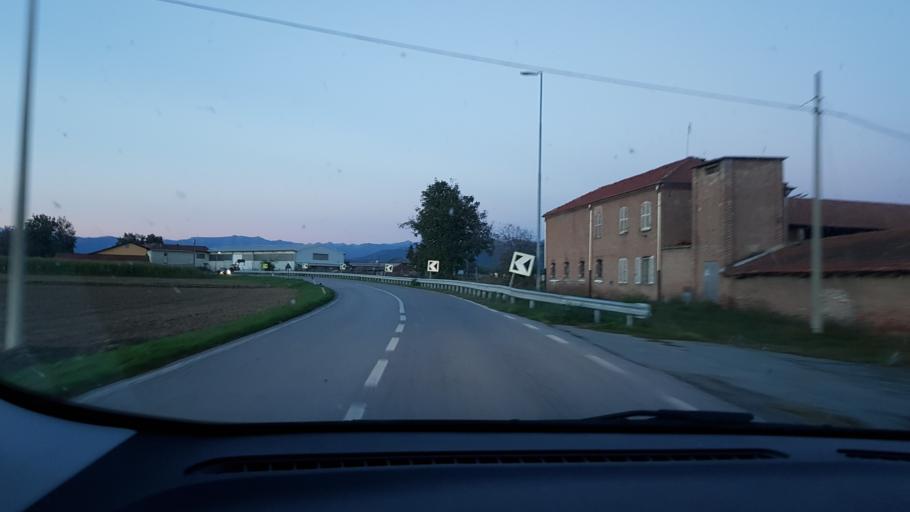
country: IT
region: Piedmont
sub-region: Provincia di Cuneo
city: Vottignasco
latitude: 44.5600
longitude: 7.5675
